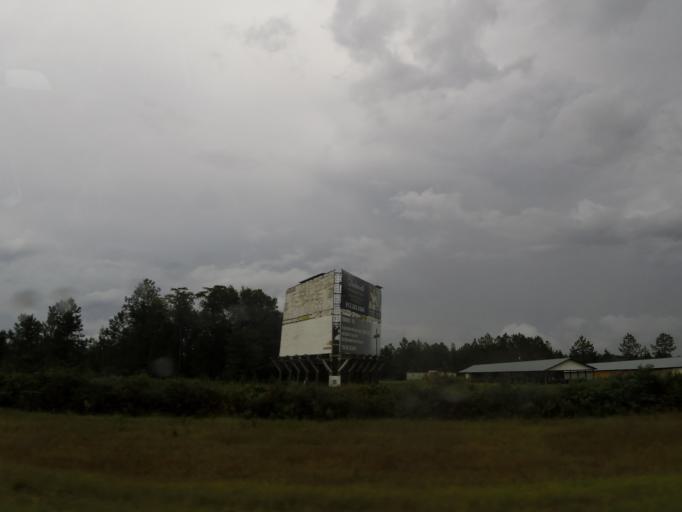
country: US
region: Georgia
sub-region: Wayne County
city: Jesup
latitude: 31.4760
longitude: -81.7269
